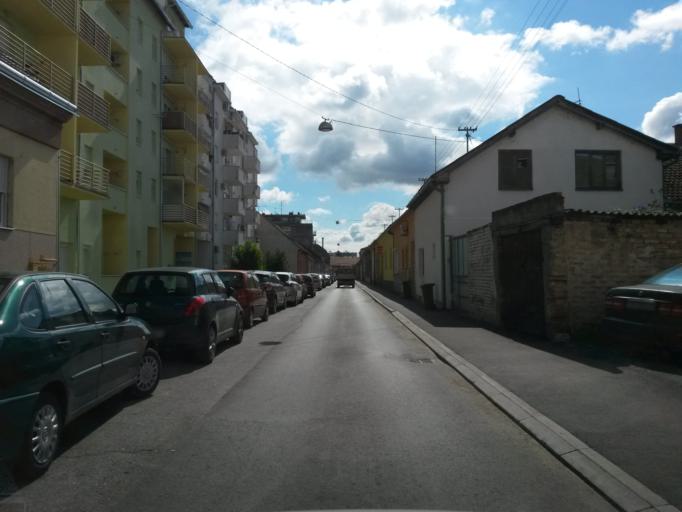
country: HR
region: Osjecko-Baranjska
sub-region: Grad Osijek
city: Osijek
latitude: 45.5601
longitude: 18.6740
